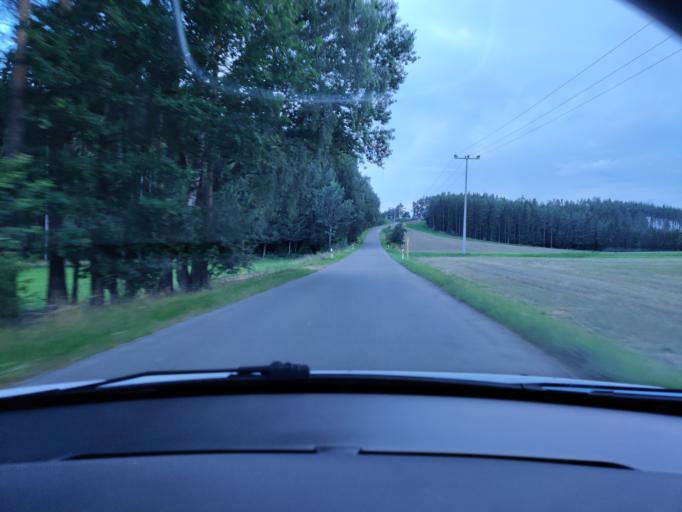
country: DE
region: Bavaria
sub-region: Upper Palatinate
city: Pfreimd
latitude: 49.4800
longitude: 12.1460
